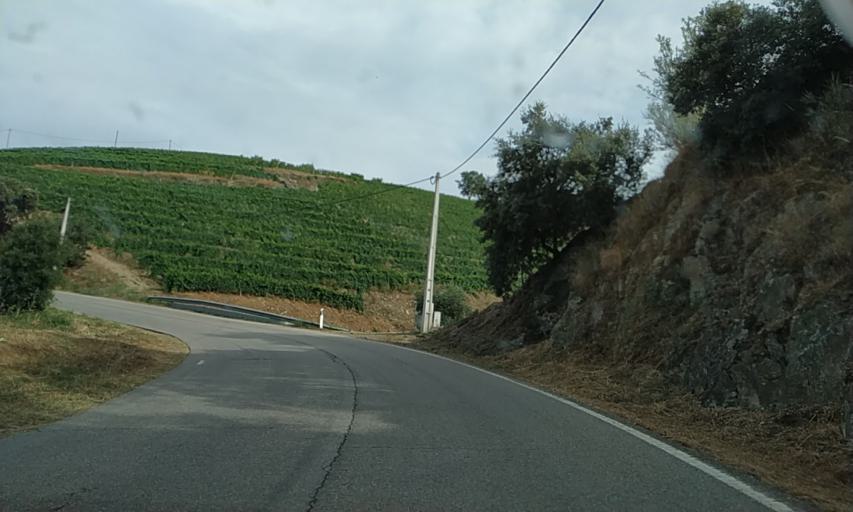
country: PT
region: Viseu
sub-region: Sao Joao da Pesqueira
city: Sao Joao da Pesqueira
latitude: 41.0804
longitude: -7.3934
